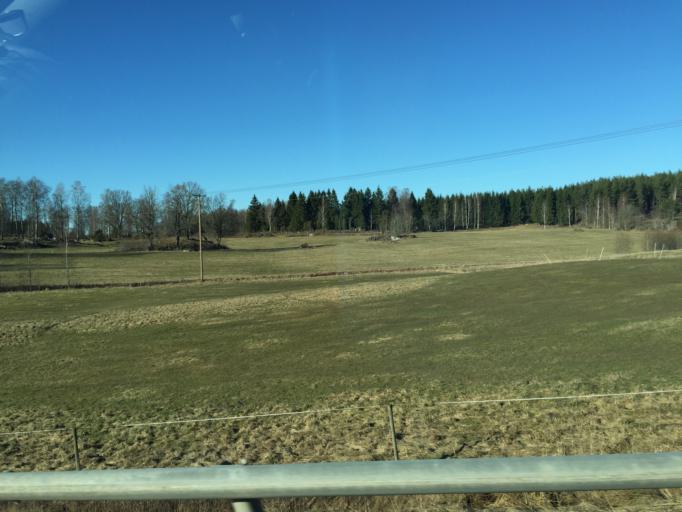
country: SE
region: OEstergoetland
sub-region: Finspangs Kommun
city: Finspang
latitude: 58.7201
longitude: 15.6560
